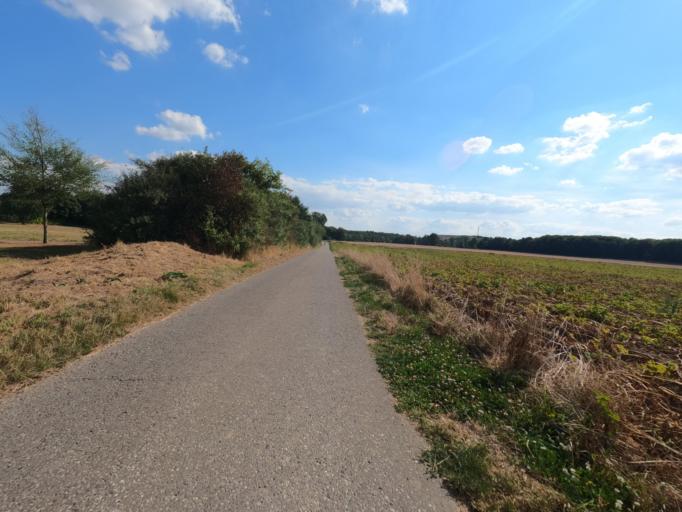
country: DE
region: North Rhine-Westphalia
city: Huckelhoven
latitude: 51.0957
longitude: 6.2042
